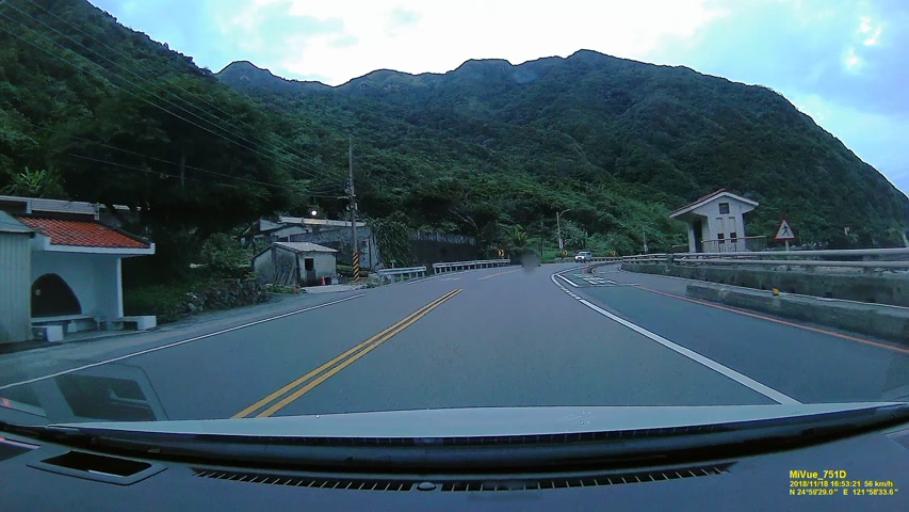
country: TW
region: Taiwan
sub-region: Keelung
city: Keelung
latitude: 24.9905
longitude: 121.9752
